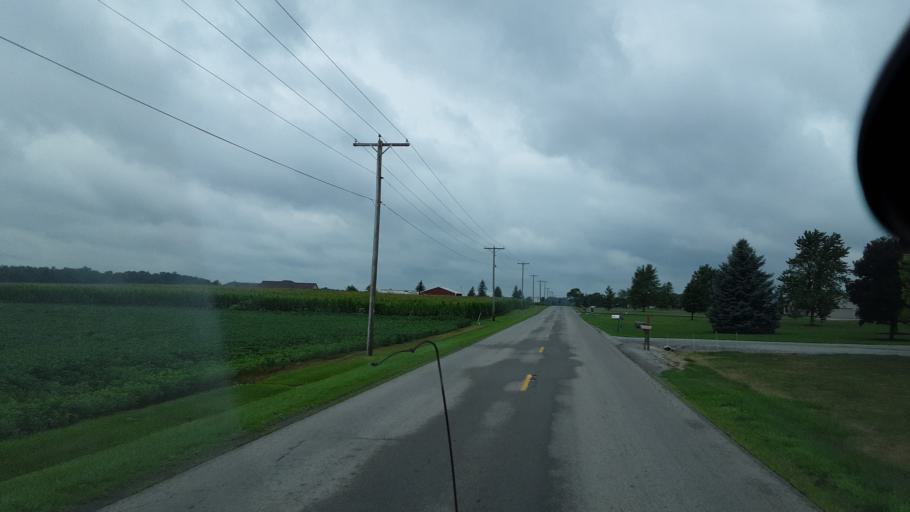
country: US
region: Indiana
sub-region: Allen County
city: New Haven
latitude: 40.9472
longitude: -85.0305
